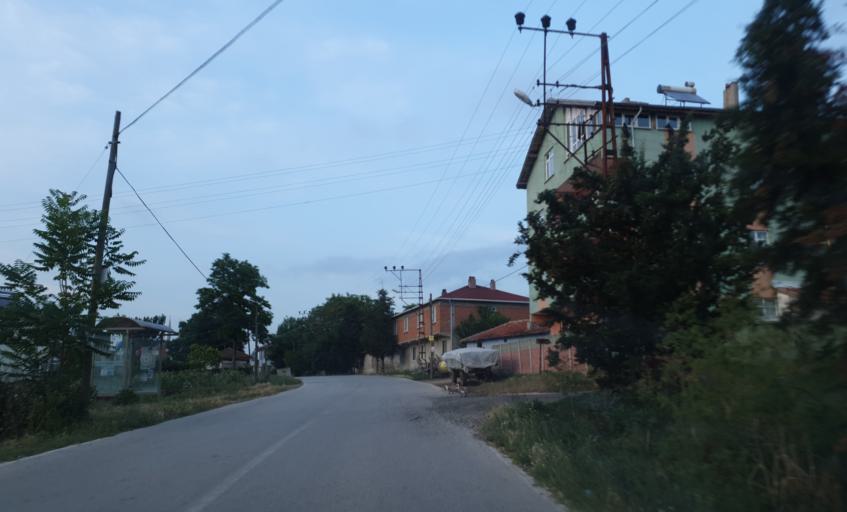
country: TR
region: Tekirdag
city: Beyazkoy
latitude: 41.3813
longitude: 27.6161
